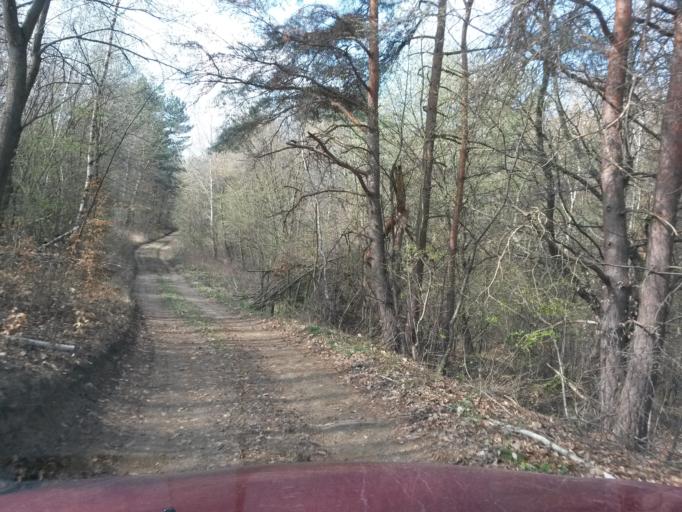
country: SK
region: Presovsky
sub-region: Okres Presov
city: Presov
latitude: 48.9264
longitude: 21.1461
